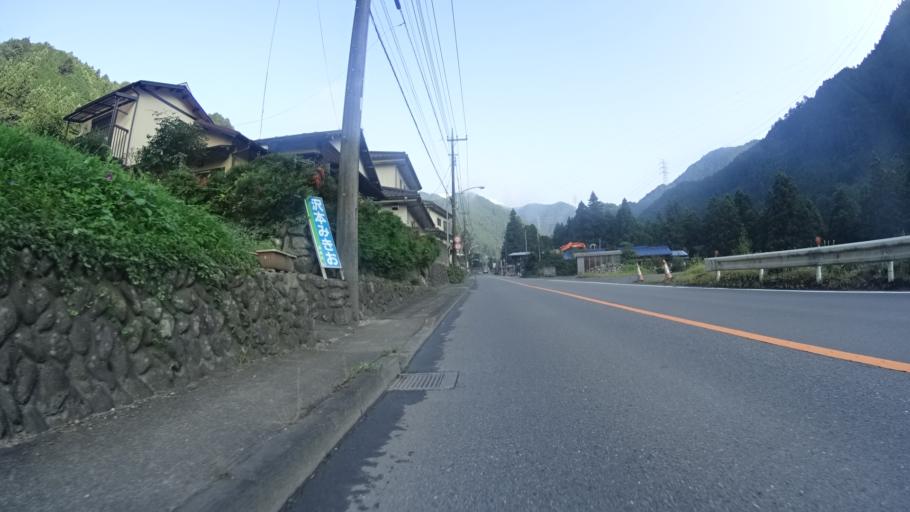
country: JP
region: Tokyo
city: Ome
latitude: 35.8092
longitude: 139.1675
